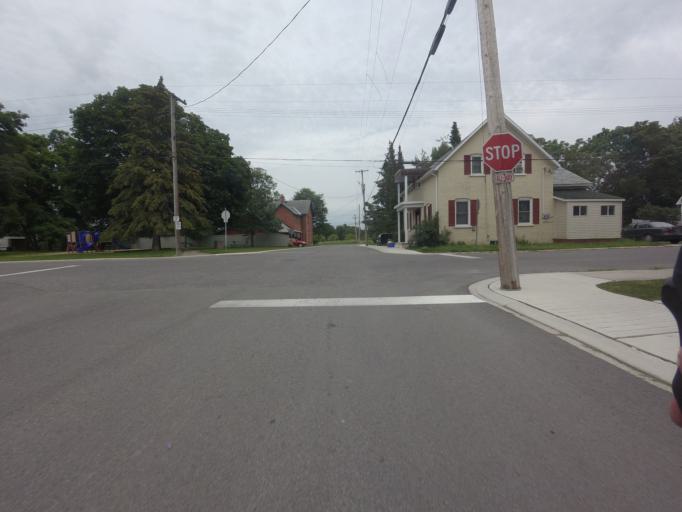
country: CA
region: Ontario
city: Carleton Place
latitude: 45.1413
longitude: -76.1508
